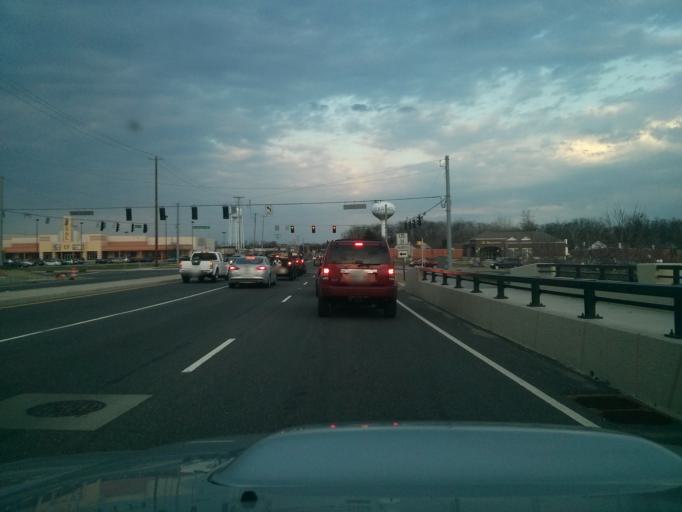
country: US
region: Indiana
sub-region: Hamilton County
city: Carmel
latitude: 40.0001
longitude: -86.1237
